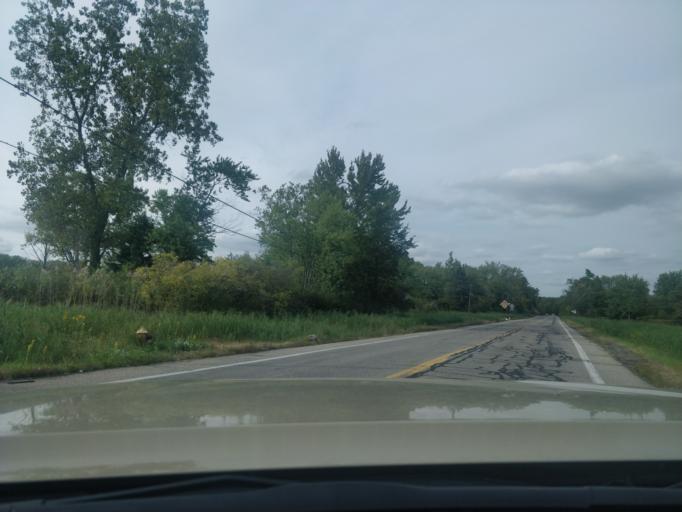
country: US
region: Michigan
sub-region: Wayne County
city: Romulus
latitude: 42.1803
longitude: -83.3705
